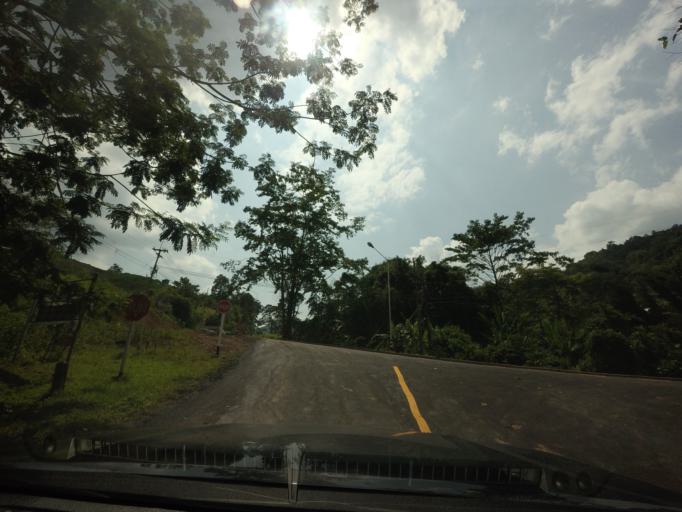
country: TH
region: Nan
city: Bo Kluea
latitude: 19.1965
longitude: 101.1833
